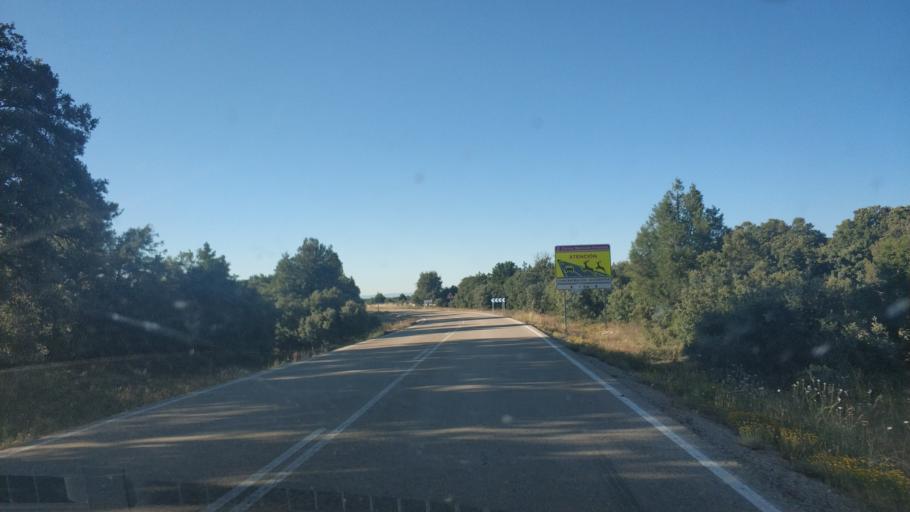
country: ES
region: Castille and Leon
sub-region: Provincia de Soria
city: Liceras
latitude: 41.4566
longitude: -3.2113
